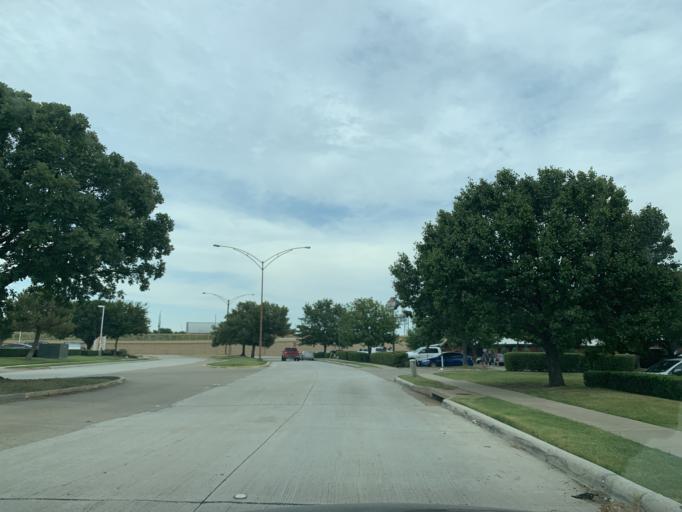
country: US
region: Texas
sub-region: Tarrant County
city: Watauga
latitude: 32.8379
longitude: -97.2936
